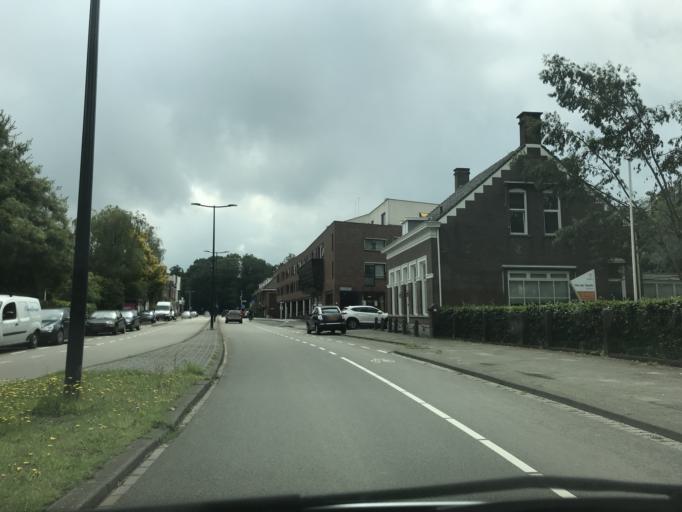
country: NL
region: North Brabant
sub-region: Gemeente Breda
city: Breda
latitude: 51.5679
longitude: 4.7732
